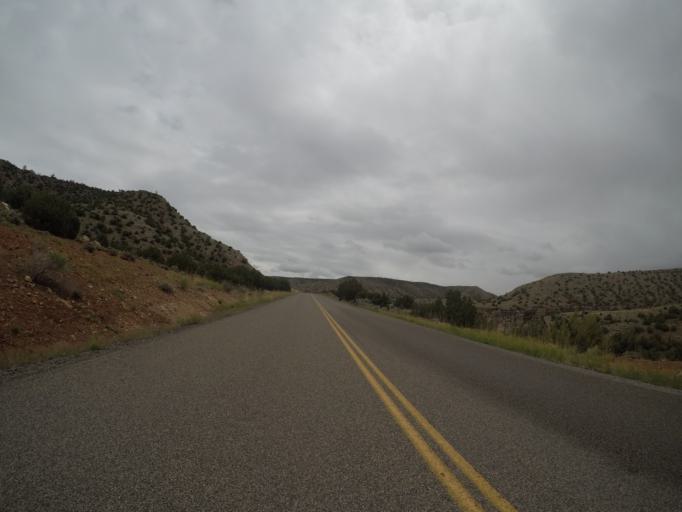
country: US
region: Wyoming
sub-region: Big Horn County
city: Lovell
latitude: 45.0999
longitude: -108.2179
